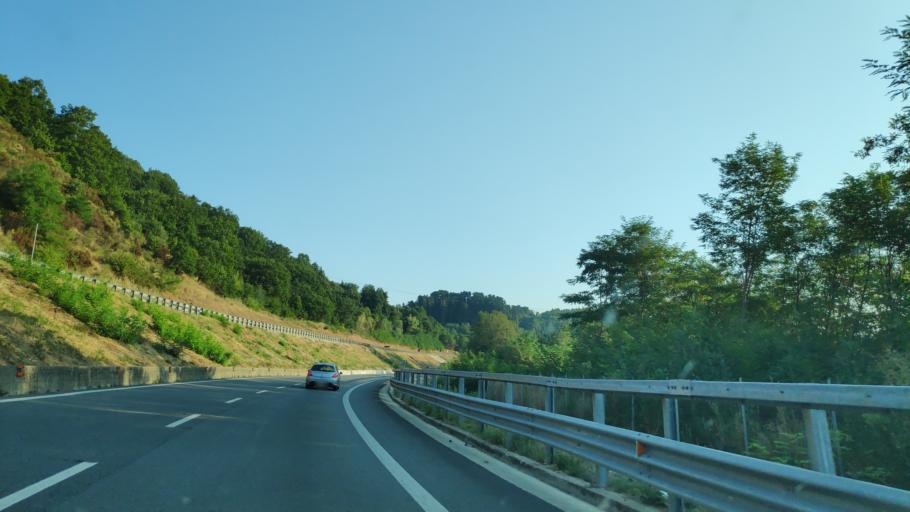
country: IT
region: Calabria
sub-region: Provincia di Cosenza
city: Belsito
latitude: 39.1591
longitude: 16.2868
